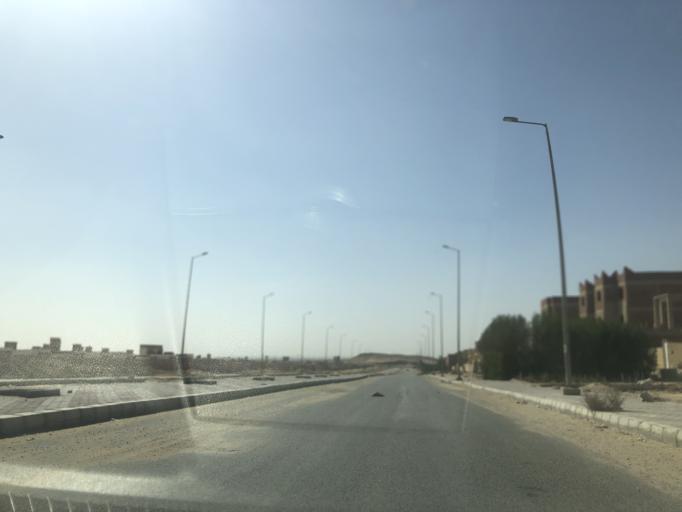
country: EG
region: Al Jizah
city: Madinat Sittah Uktubar
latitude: 29.9310
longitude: 30.9649
